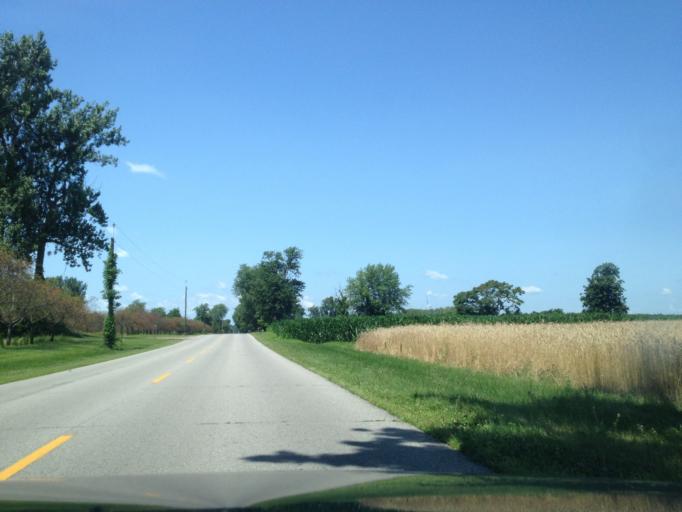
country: CA
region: Ontario
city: Aylmer
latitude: 42.6139
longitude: -80.6969
